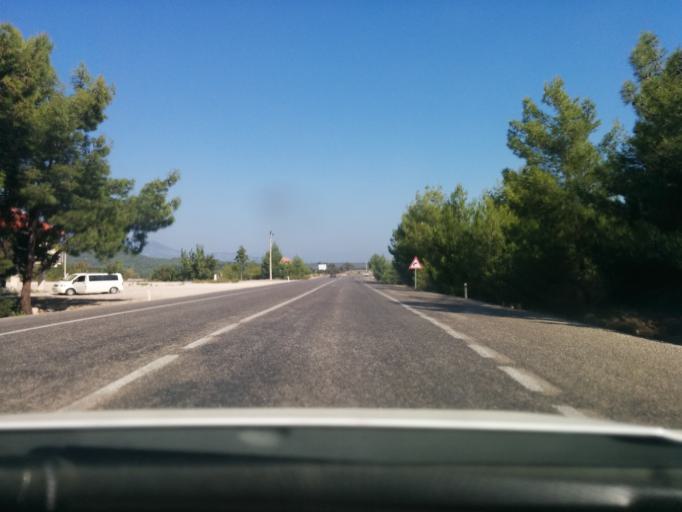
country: TR
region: Mugla
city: Esen
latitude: 36.3806
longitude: 29.3222
